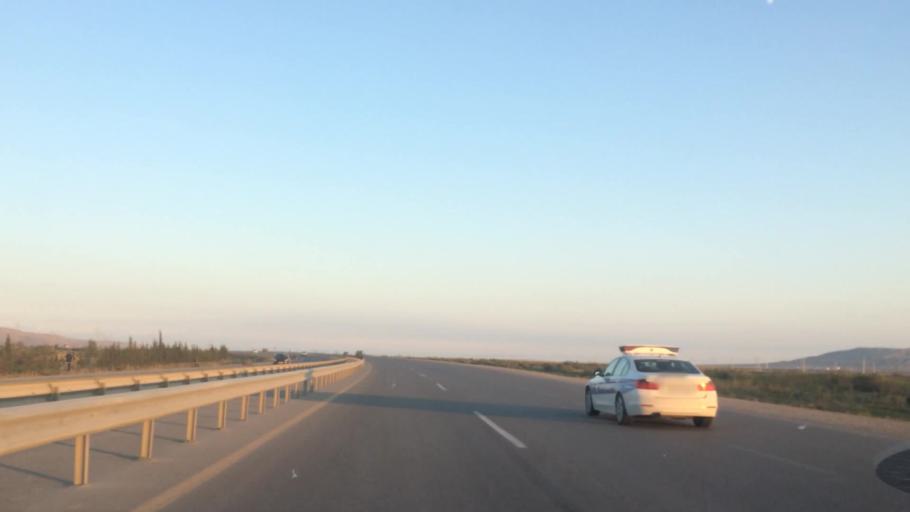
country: AZ
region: Baki
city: Qobustan
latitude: 39.9842
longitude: 49.2130
